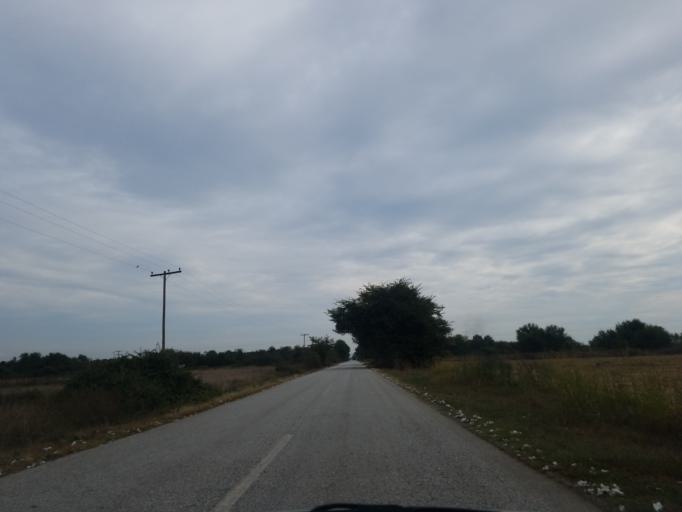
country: GR
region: Thessaly
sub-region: Nomos Kardhitsas
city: Agia Triada
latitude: 39.4613
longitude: 21.8779
